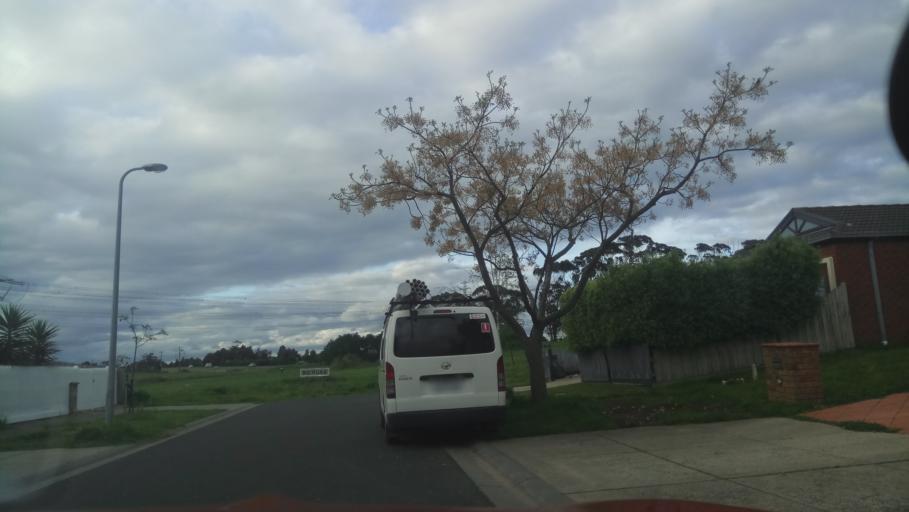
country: AU
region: Victoria
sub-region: Casey
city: Lynbrook
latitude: -38.0672
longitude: 145.2653
